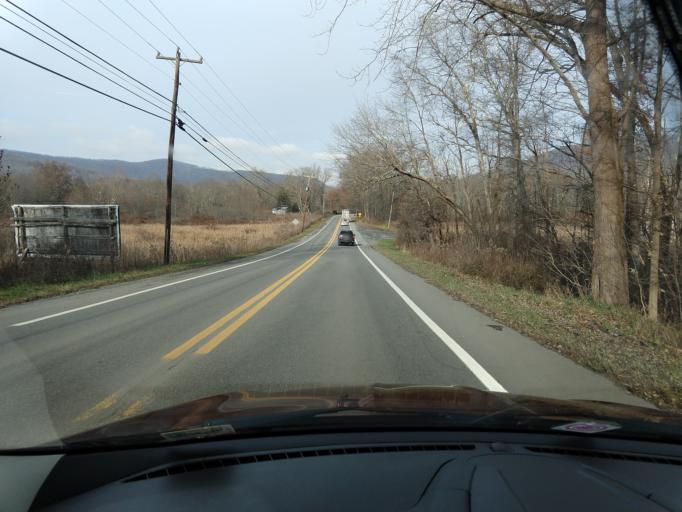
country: US
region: West Virginia
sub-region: Greenbrier County
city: Rainelle
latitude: 37.9552
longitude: -80.6797
